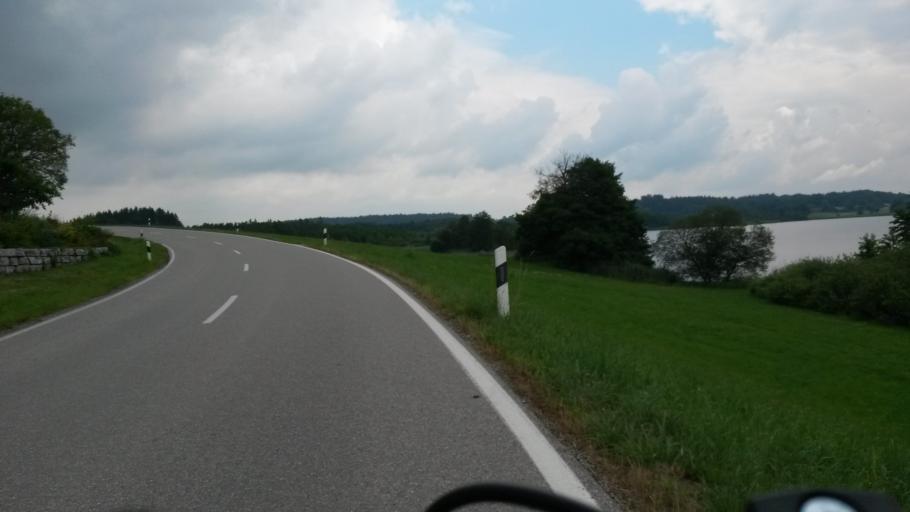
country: DE
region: Bavaria
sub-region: Upper Bavaria
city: Hoslwang
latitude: 47.9340
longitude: 12.3434
